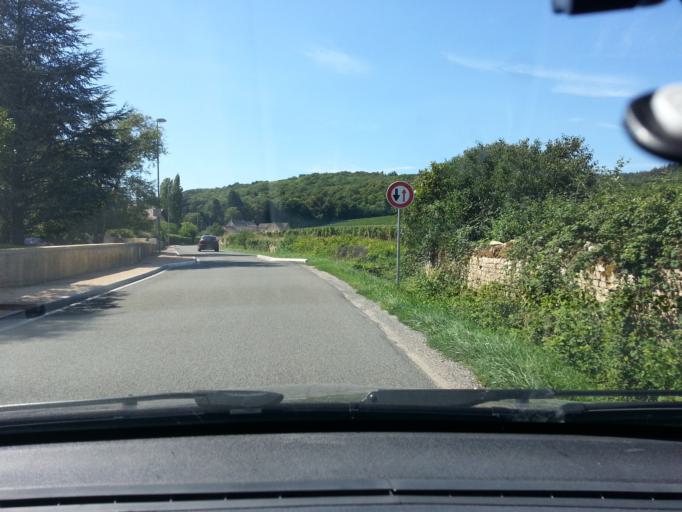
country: FR
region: Bourgogne
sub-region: Departement de Saone-et-Loire
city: Givry
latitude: 46.7800
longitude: 4.7358
